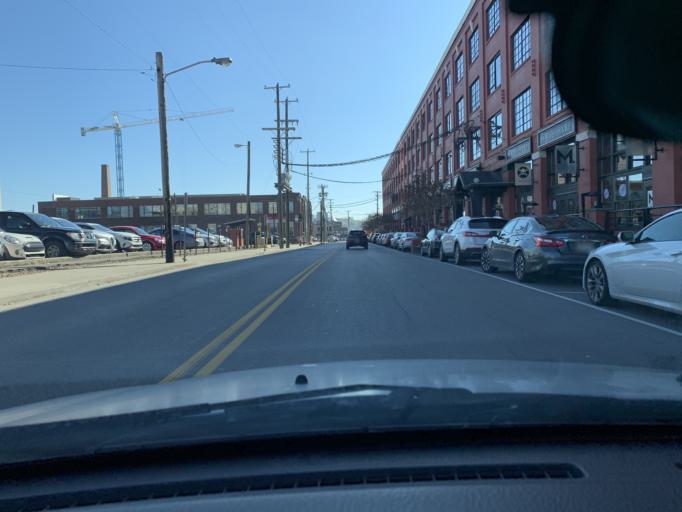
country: US
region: Tennessee
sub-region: Davidson County
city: Nashville
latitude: 36.1557
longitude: -86.7825
